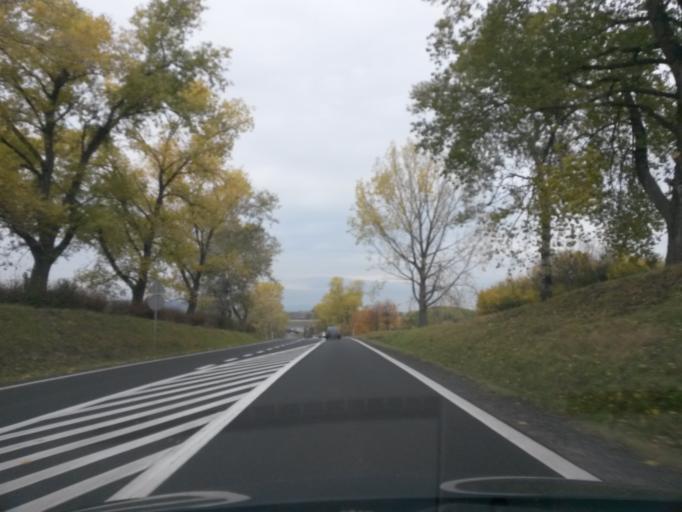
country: PL
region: Lower Silesian Voivodeship
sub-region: Powiat dzierzoniowski
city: Niemcza
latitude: 50.6717
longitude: 16.8310
